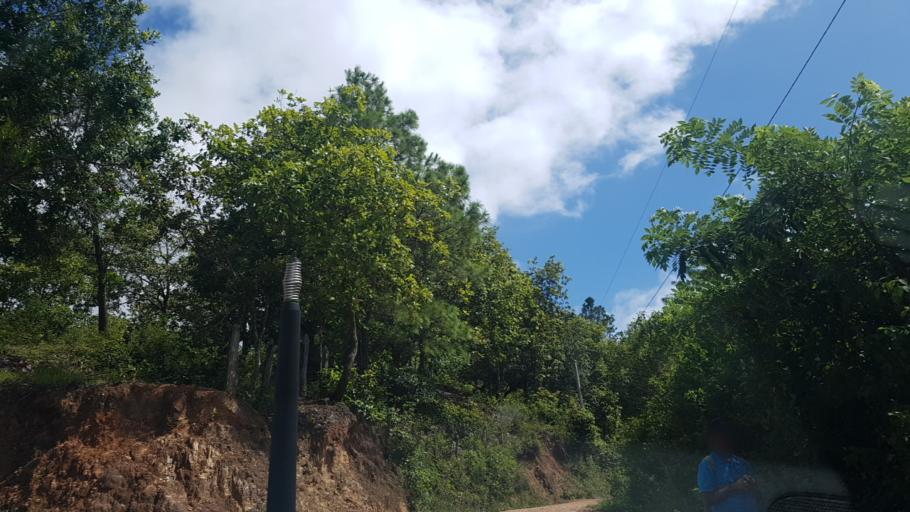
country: NI
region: Nueva Segovia
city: Ciudad Antigua
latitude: 13.6456
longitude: -86.2700
